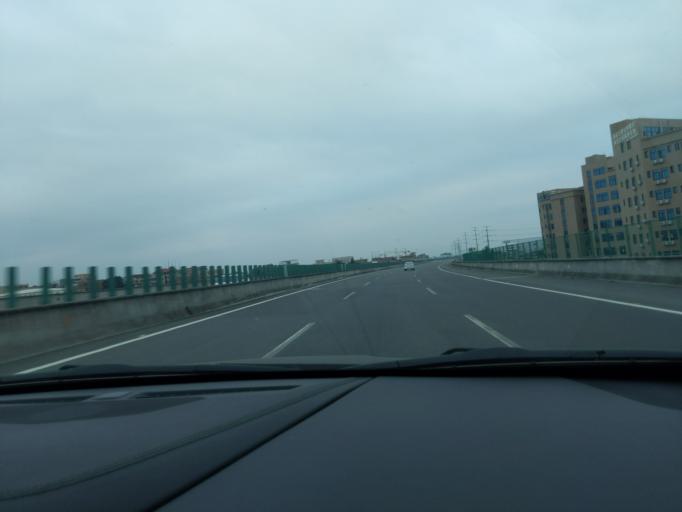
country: CN
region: Fujian
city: Shishi
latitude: 24.7623
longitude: 118.6131
